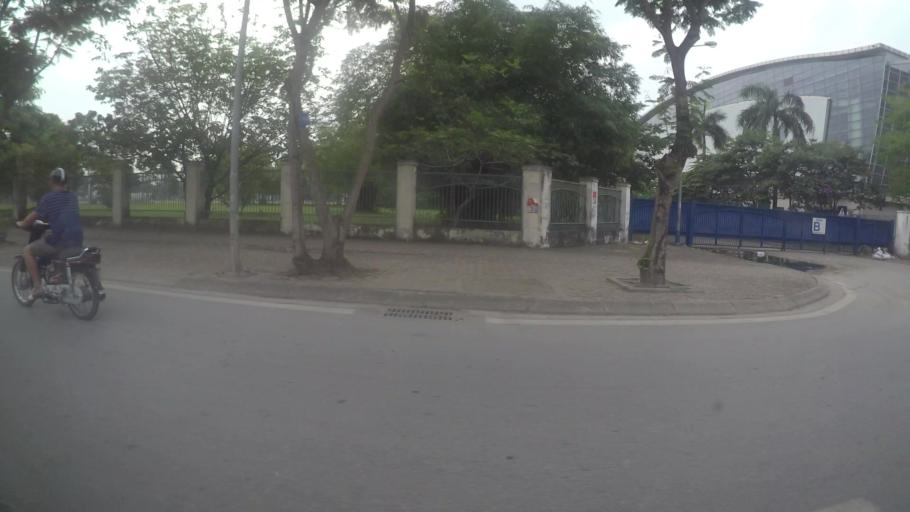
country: VN
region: Ha Noi
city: Cau Dien
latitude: 21.0276
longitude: 105.7634
